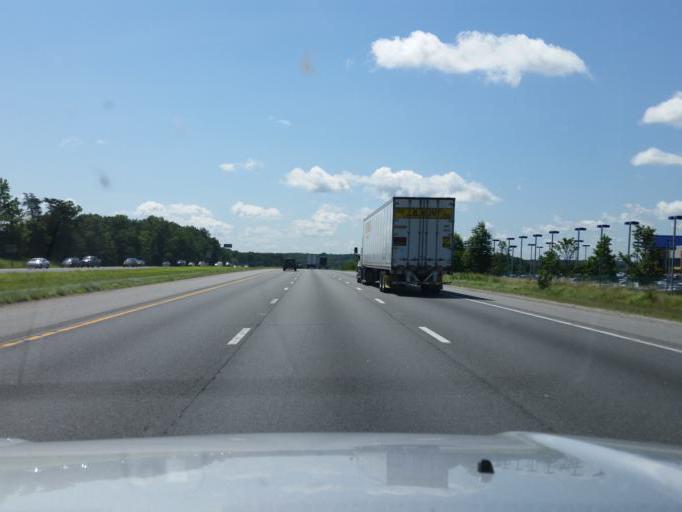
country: US
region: Virginia
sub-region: City of Fredericksburg
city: Fredericksburg
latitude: 38.2470
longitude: -77.5066
